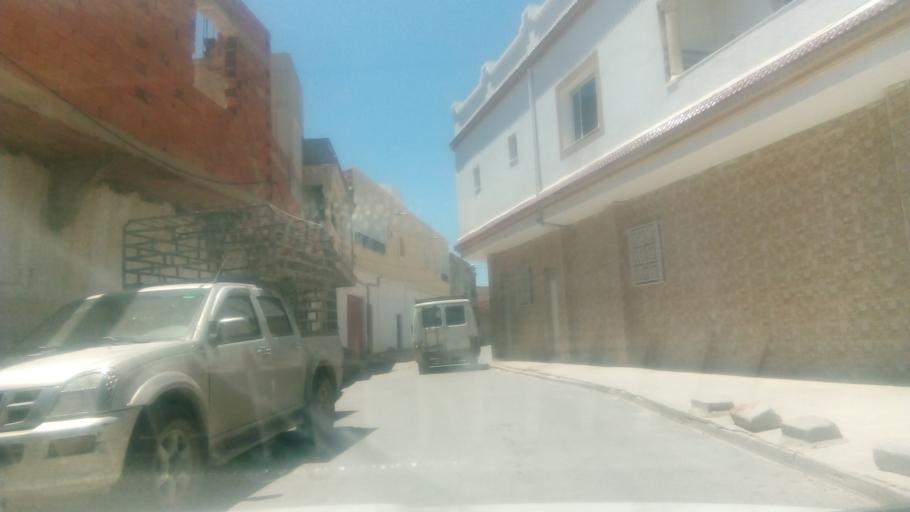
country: TN
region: Al Qayrawan
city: Kairouan
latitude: 35.6670
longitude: 10.0887
